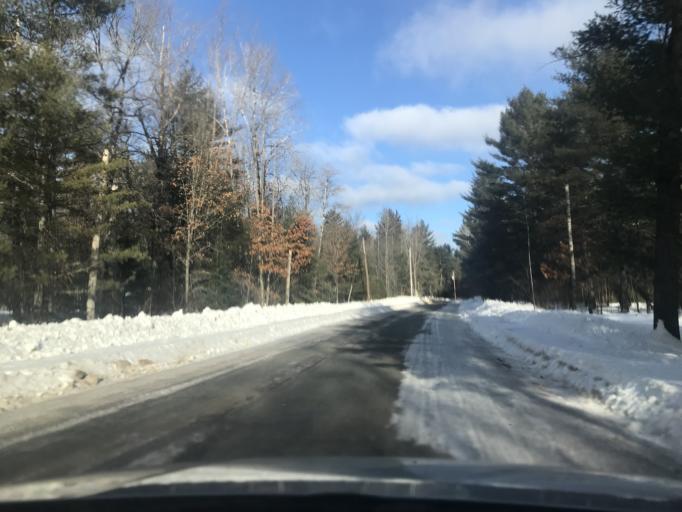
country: US
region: Wisconsin
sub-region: Marinette County
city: Niagara
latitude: 45.6358
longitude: -87.9695
